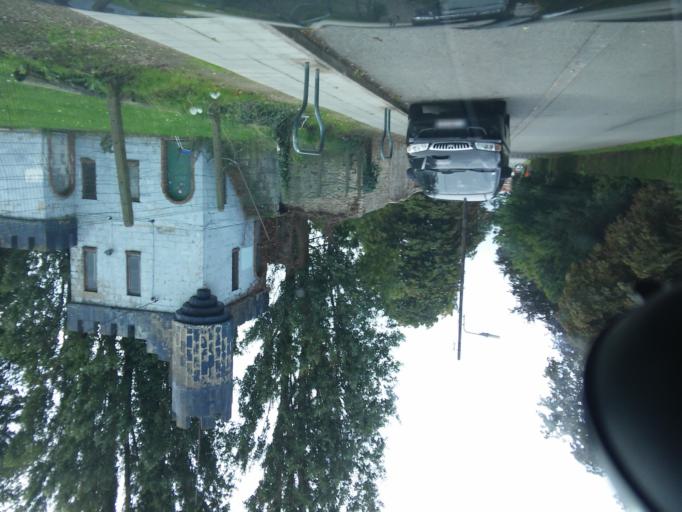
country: BE
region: Flanders
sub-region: Provincie Vlaams-Brabant
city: Steenokkerzeel
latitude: 50.9131
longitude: 4.5119
